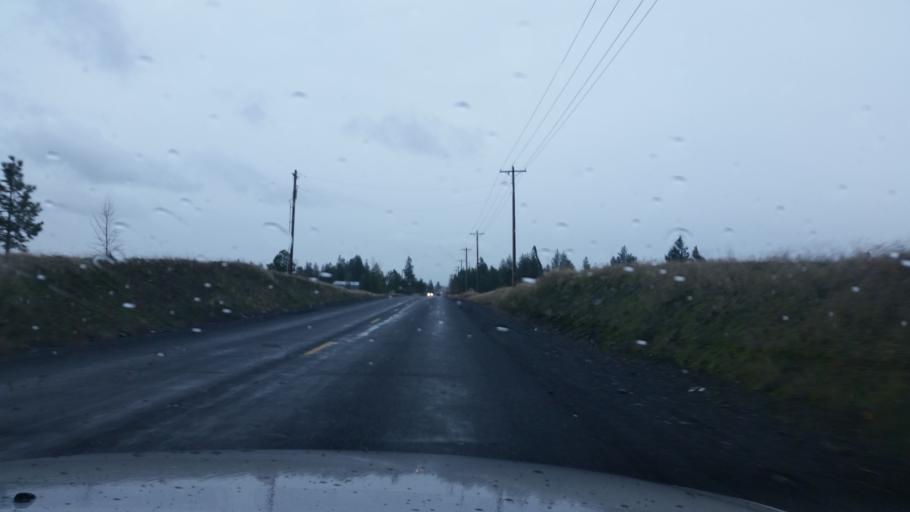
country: US
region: Washington
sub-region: Spokane County
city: Airway Heights
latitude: 47.6719
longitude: -117.5927
